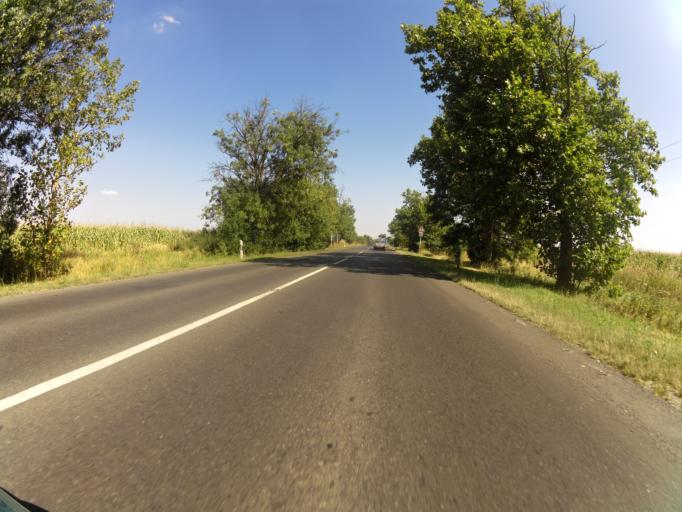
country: HU
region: Csongrad
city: Szatymaz
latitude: 46.2998
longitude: 20.0747
